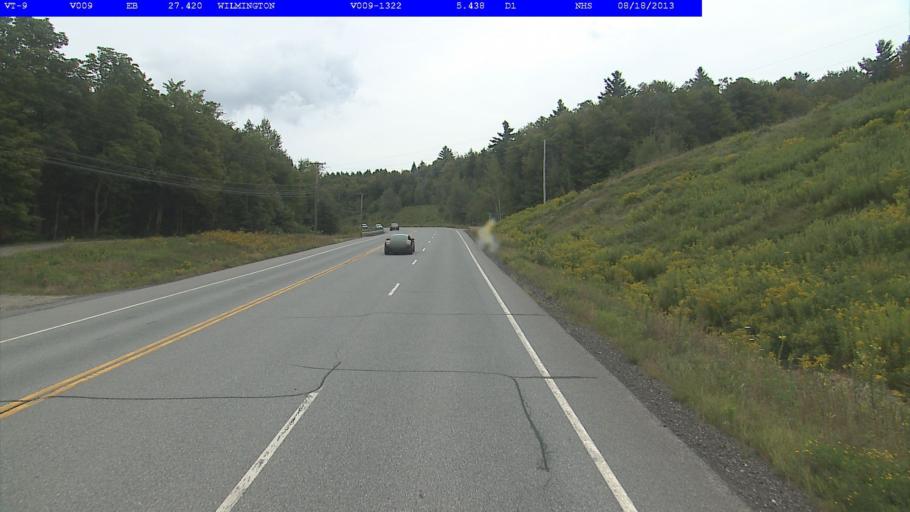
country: US
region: Vermont
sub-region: Windham County
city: Dover
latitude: 42.8534
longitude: -72.8318
